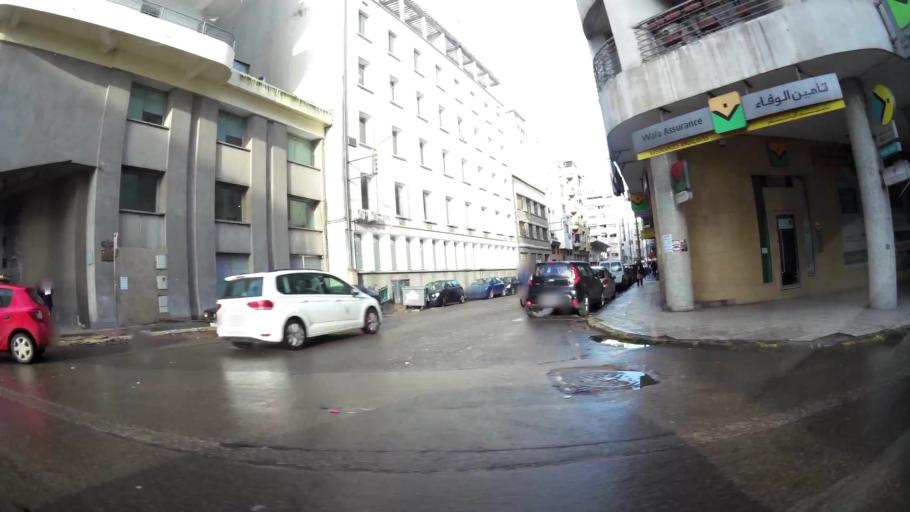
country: MA
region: Grand Casablanca
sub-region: Casablanca
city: Casablanca
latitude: 33.5944
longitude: -7.6088
